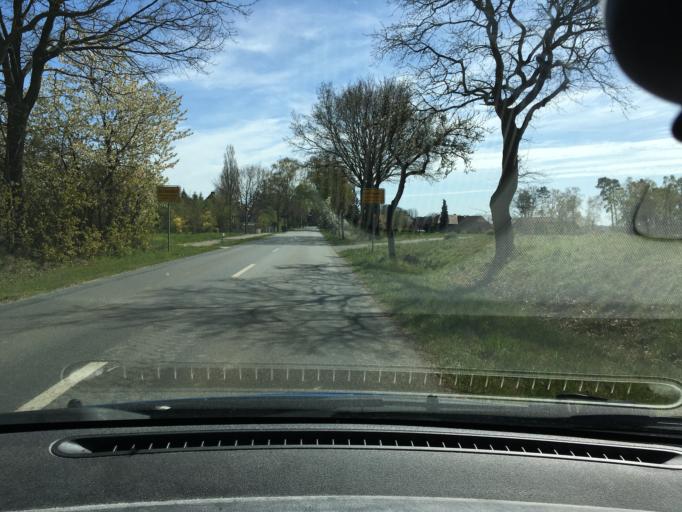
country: DE
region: Lower Saxony
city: Himbergen
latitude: 53.1313
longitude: 10.6929
